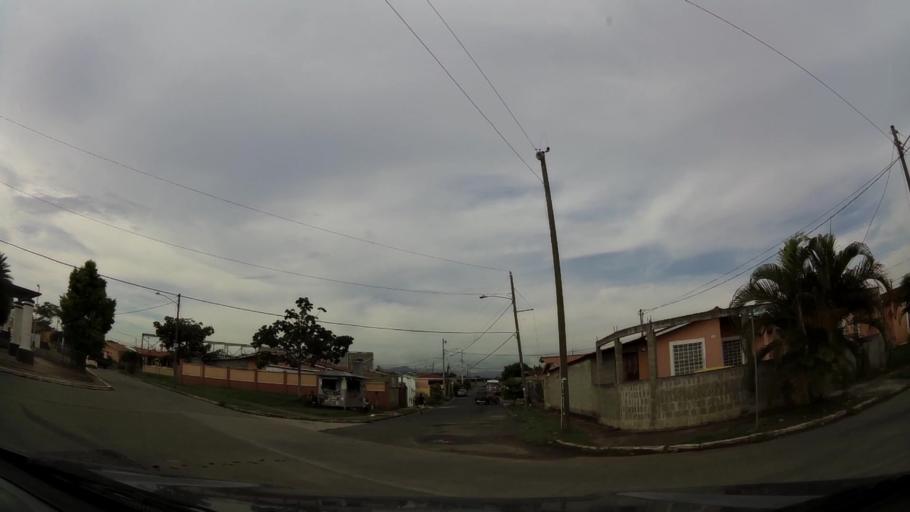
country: PA
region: Panama
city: Tocumen
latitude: 9.0739
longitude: -79.3631
